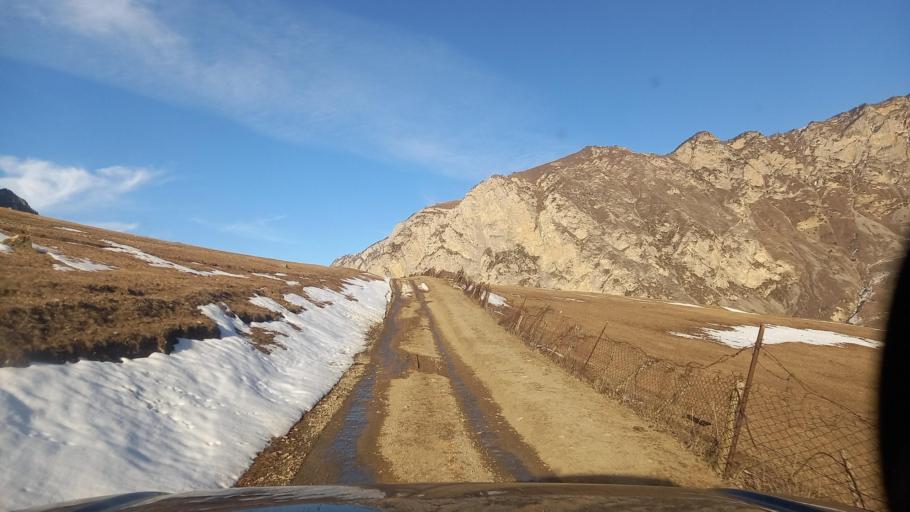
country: RU
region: Ingushetiya
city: Dzhayrakh
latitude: 42.8511
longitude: 44.5140
